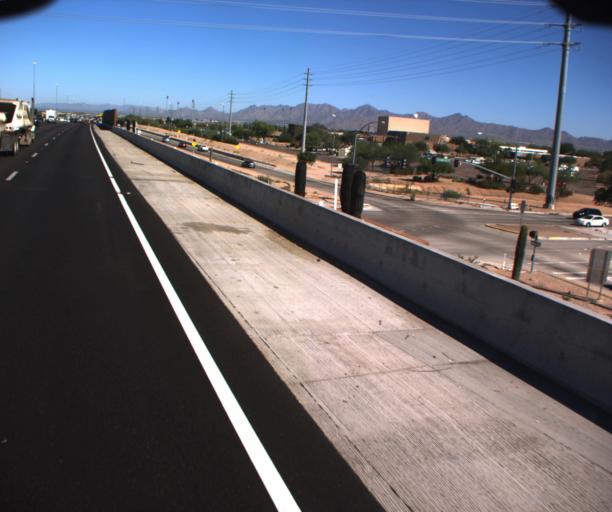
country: US
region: Arizona
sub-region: Maricopa County
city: Scottsdale
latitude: 33.5089
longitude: -111.8877
